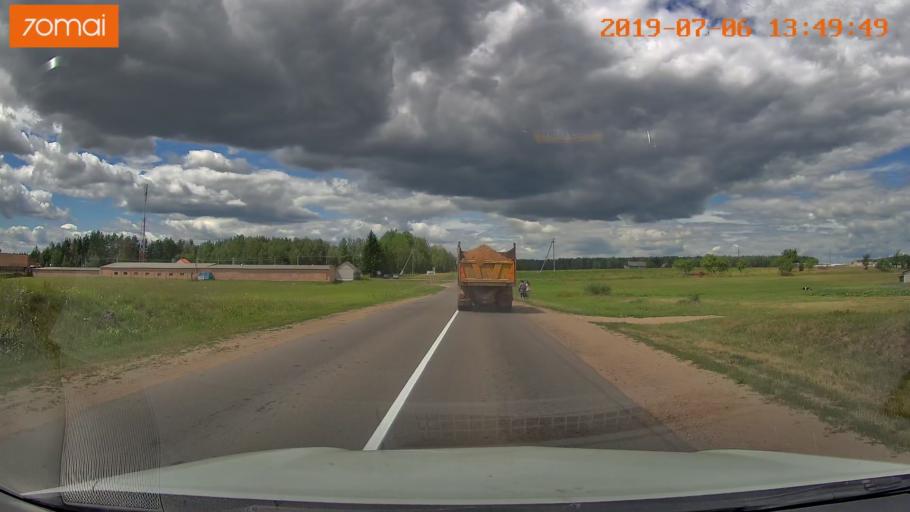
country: BY
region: Minsk
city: Ivyanyets
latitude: 53.6955
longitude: 26.8495
